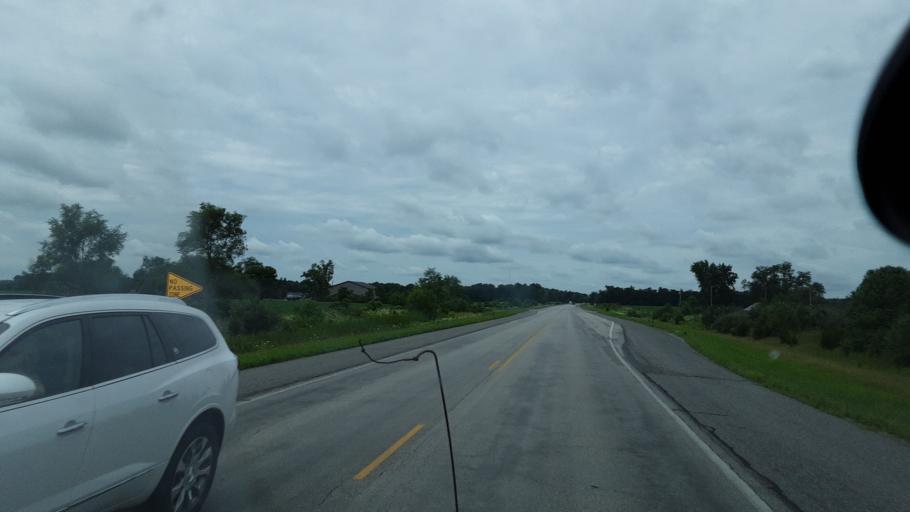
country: US
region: Indiana
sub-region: Adams County
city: Decatur
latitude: 40.8032
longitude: -84.9151
